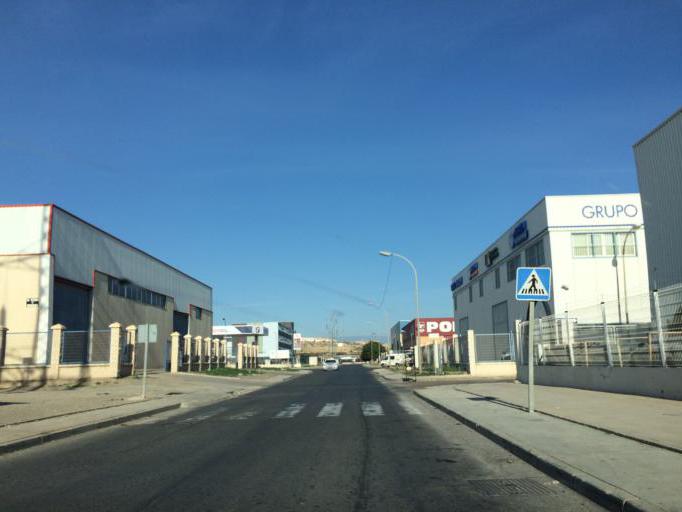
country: ES
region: Andalusia
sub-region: Provincia de Almeria
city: Almeria
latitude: 36.8525
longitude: -2.4310
